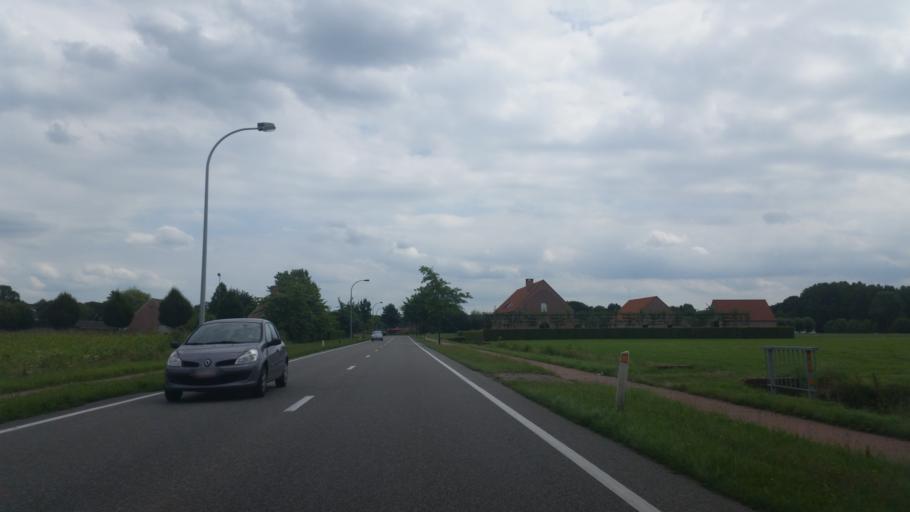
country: BE
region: Flanders
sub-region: Provincie Antwerpen
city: Hoogstraten
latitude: 51.3891
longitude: 4.8157
